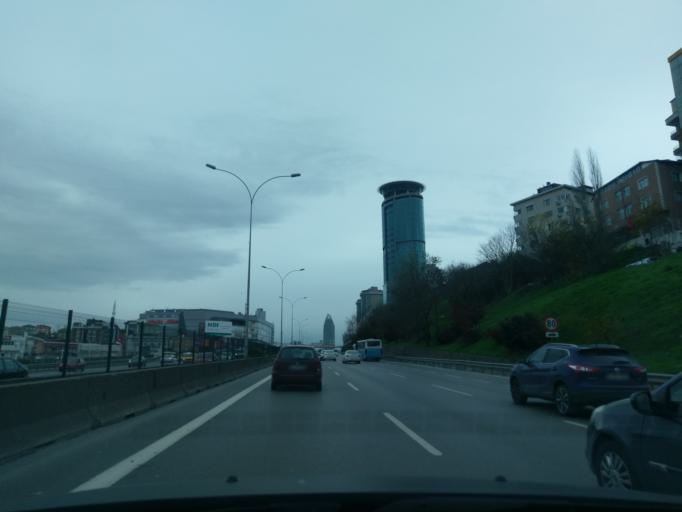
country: TR
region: Istanbul
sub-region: Atasehir
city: Atasehir
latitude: 40.9901
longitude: 29.0796
